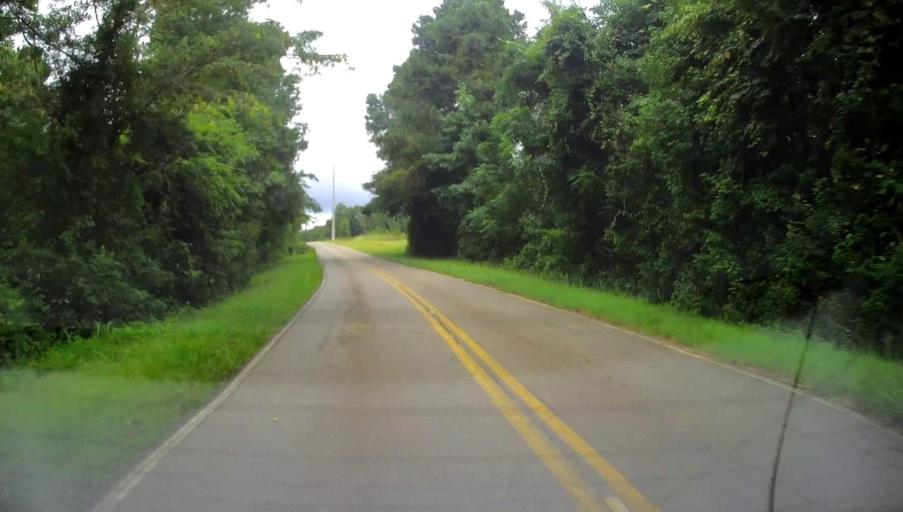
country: US
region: Georgia
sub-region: Bibb County
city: Macon
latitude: 32.7887
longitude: -83.5144
